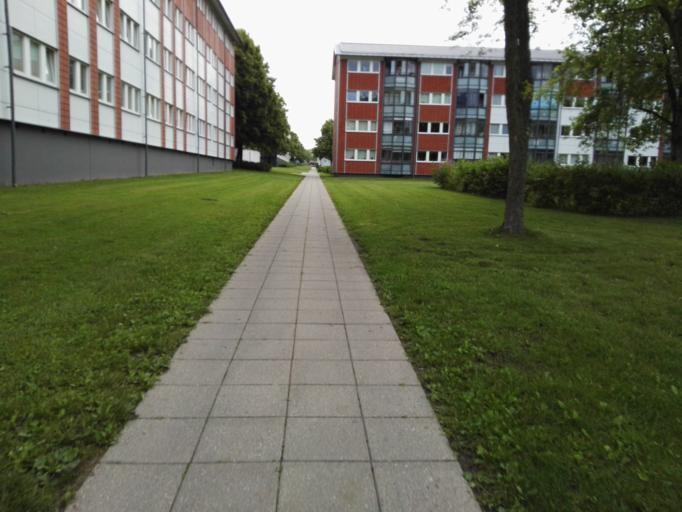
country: DK
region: Capital Region
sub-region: Ballerup Kommune
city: Ballerup
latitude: 55.7142
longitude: 12.3603
